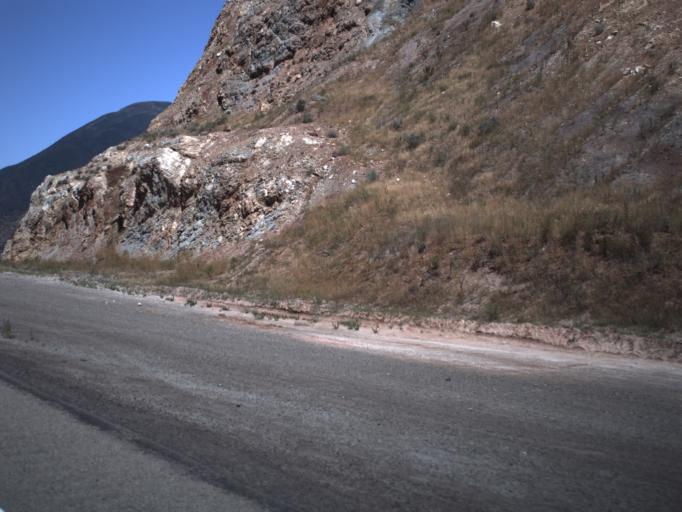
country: US
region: Utah
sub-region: Utah County
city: Mapleton
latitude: 40.0022
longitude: -111.4897
